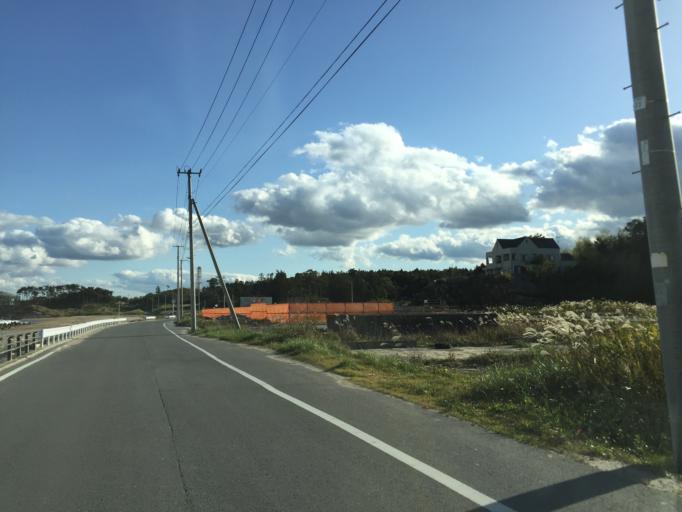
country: JP
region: Miyagi
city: Marumori
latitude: 37.8648
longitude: 140.9395
